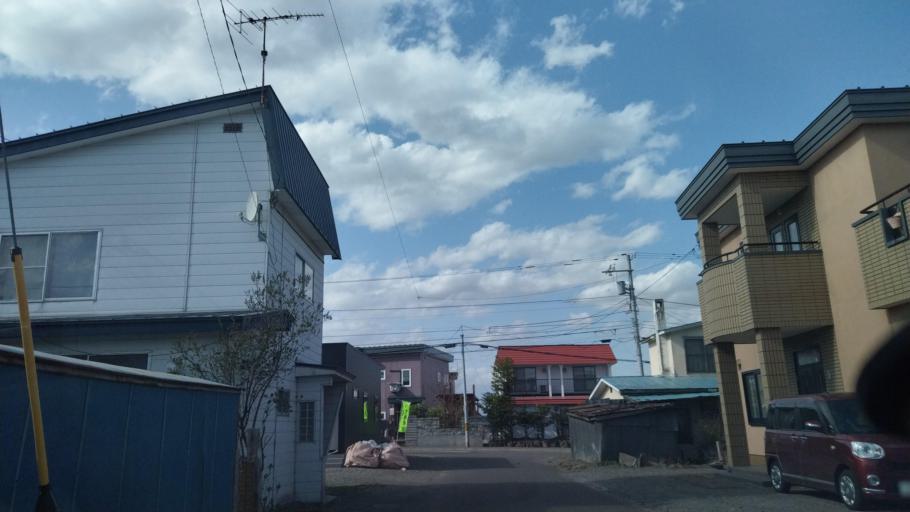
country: JP
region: Hokkaido
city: Obihiro
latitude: 42.9316
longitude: 143.1677
